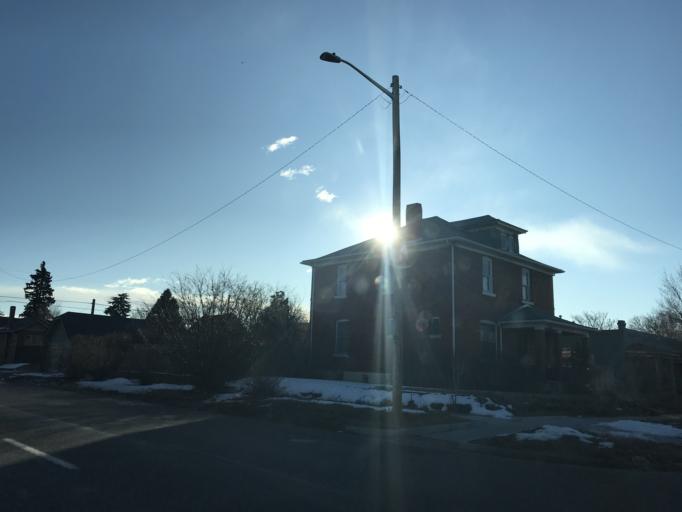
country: US
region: Colorado
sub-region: Denver County
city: Denver
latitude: 39.7608
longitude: -104.9648
